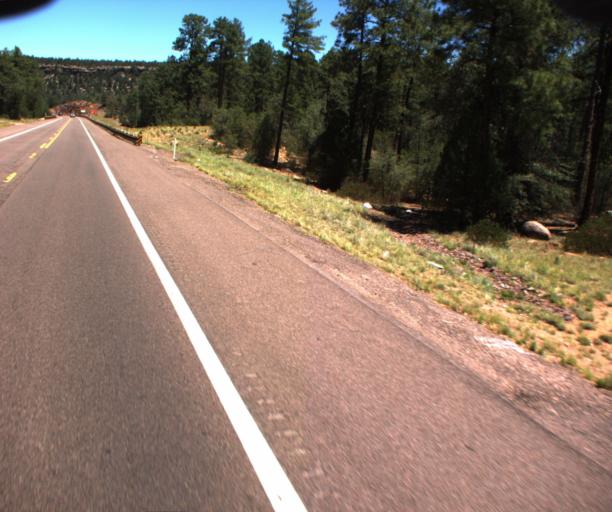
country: US
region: Arizona
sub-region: Gila County
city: Payson
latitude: 34.2722
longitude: -111.3218
